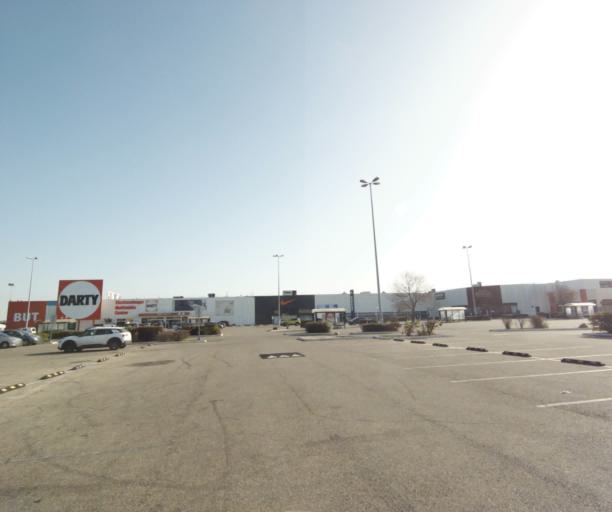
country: FR
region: Provence-Alpes-Cote d'Azur
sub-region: Departement des Bouches-du-Rhone
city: Septemes-les-Vallons
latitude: 43.4161
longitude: 5.3597
